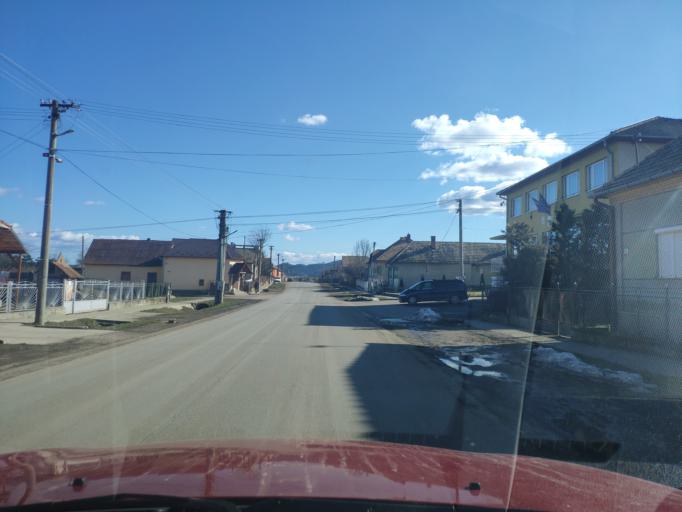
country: SK
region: Banskobystricky
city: Rimavska Sobota
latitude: 48.2886
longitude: 20.0893
